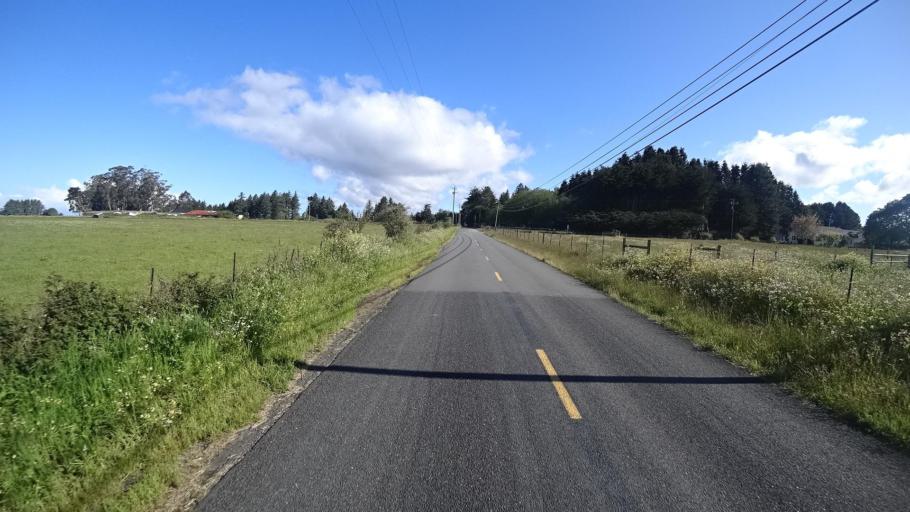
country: US
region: California
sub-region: Humboldt County
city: Westhaven-Moonstone
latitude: 41.0014
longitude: -124.1005
